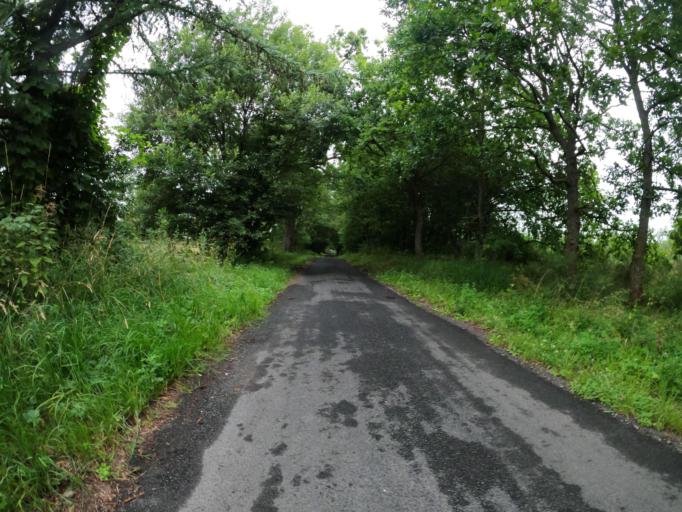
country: PL
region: West Pomeranian Voivodeship
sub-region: Powiat szczecinecki
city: Grzmiaca
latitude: 53.9539
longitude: 16.4646
